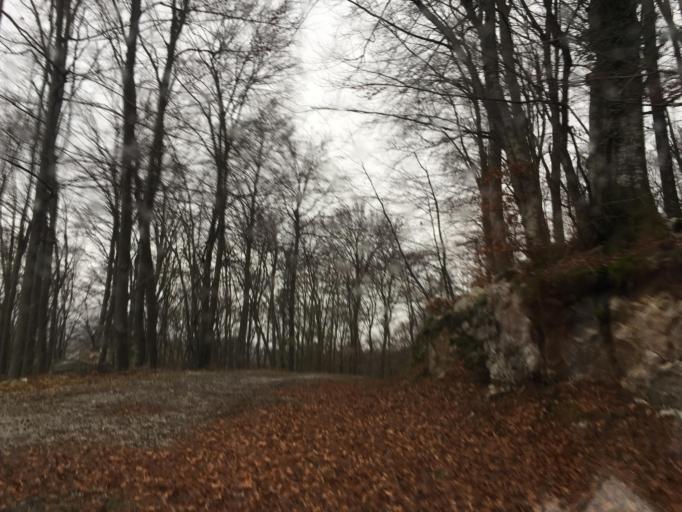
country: SI
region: Kanal
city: Kanal
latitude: 46.0663
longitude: 13.6688
